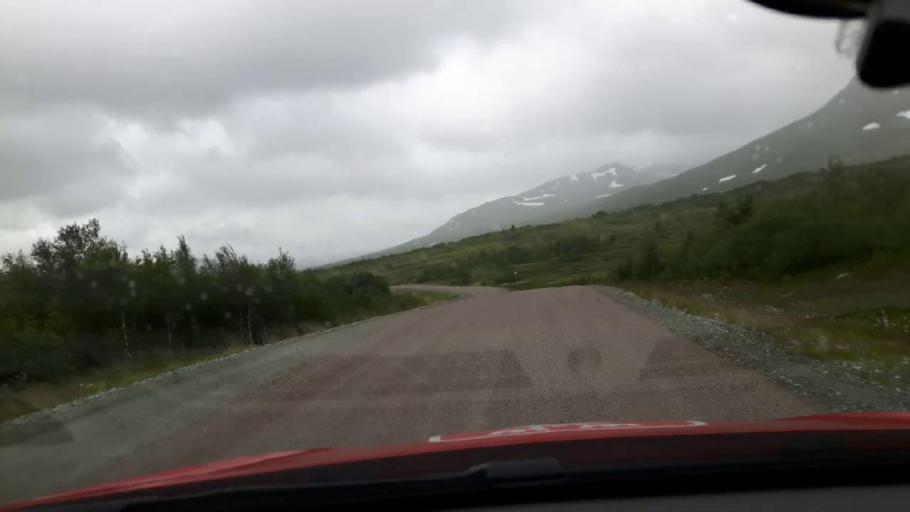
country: NO
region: Nord-Trondelag
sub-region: Meraker
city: Meraker
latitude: 63.2152
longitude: 12.4067
